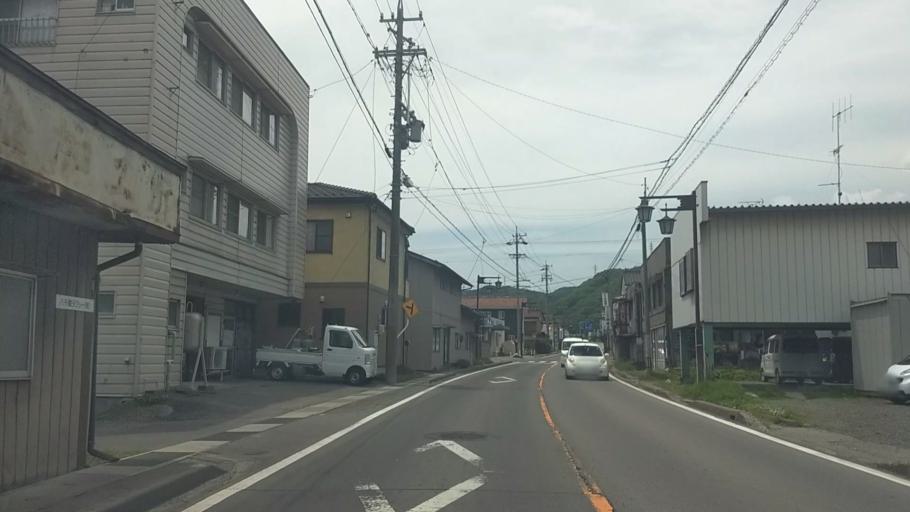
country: JP
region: Nagano
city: Saku
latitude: 36.1328
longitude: 138.4713
